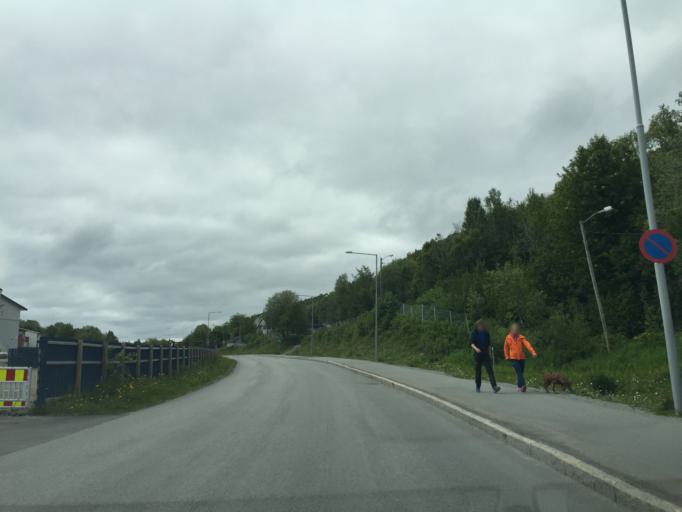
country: NO
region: Nordland
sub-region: Bodo
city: Lopsmarka
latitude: 67.2856
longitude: 14.5413
